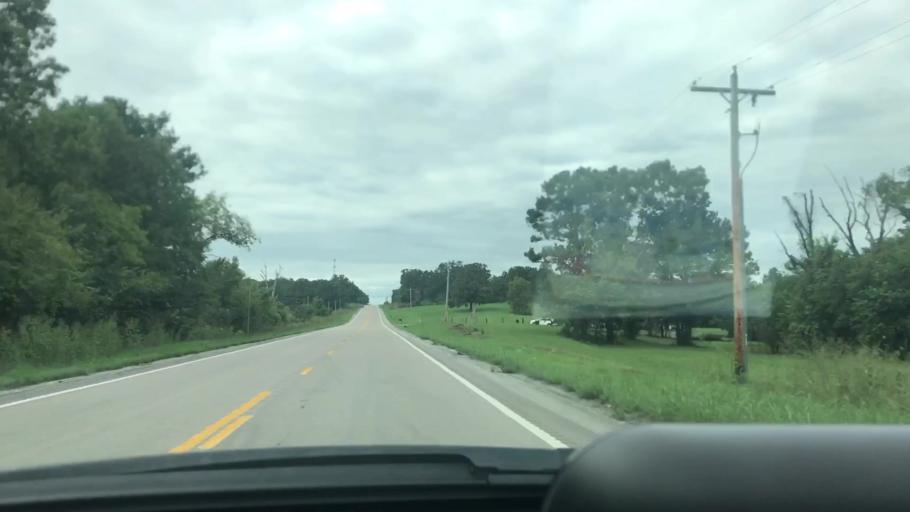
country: US
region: Missouri
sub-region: Benton County
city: Warsaw
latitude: 38.1357
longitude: -93.2826
